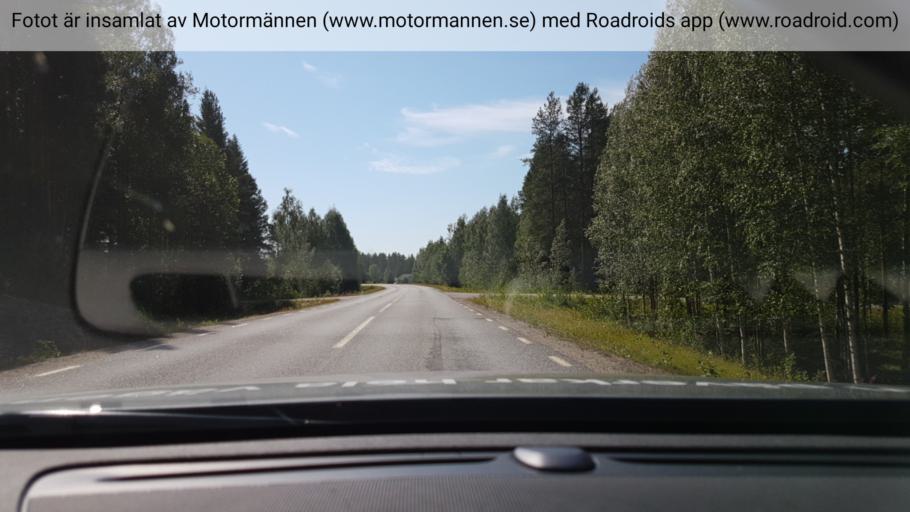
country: SE
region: Vaesterbotten
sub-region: Vindelns Kommun
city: Vindeln
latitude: 64.2890
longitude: 19.6203
